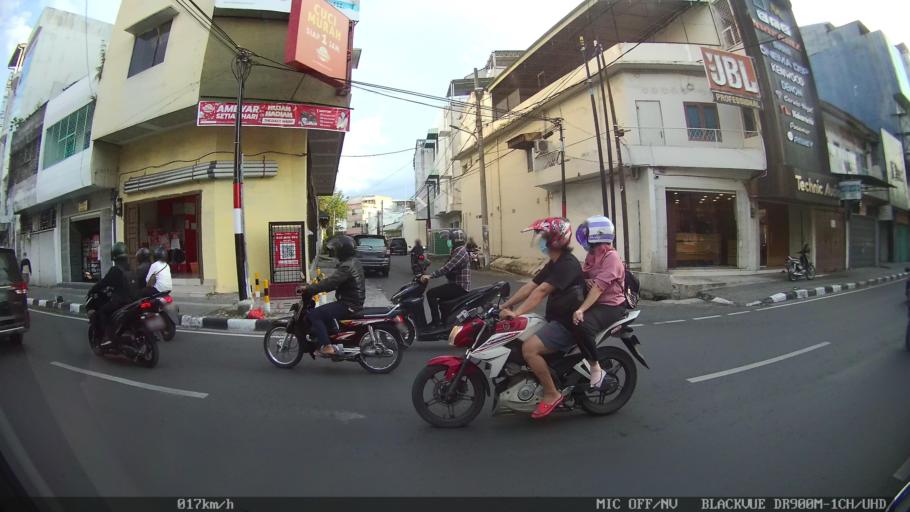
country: ID
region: North Sumatra
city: Medan
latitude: 3.5923
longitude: 98.6703
